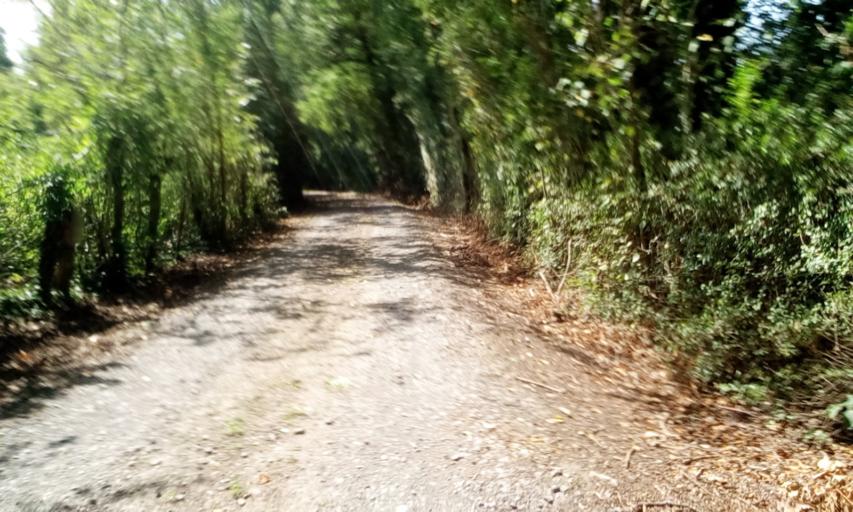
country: FR
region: Lower Normandy
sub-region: Departement du Calvados
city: Argences
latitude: 49.1344
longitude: -0.1576
